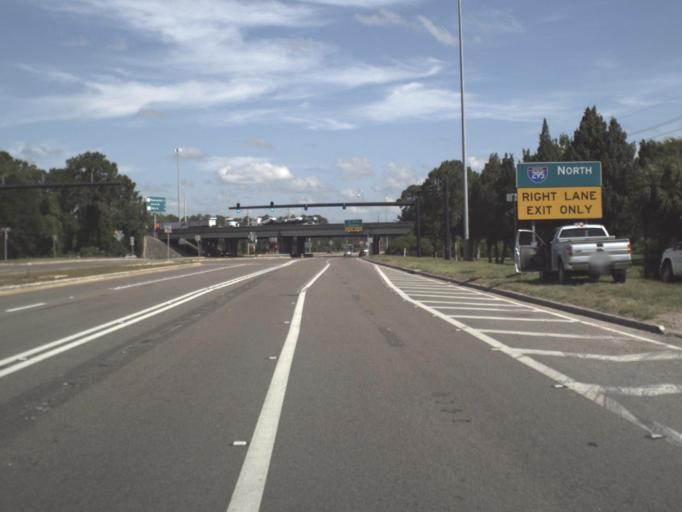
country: US
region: Florida
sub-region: Clay County
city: Orange Park
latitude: 30.1899
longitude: -81.7039
